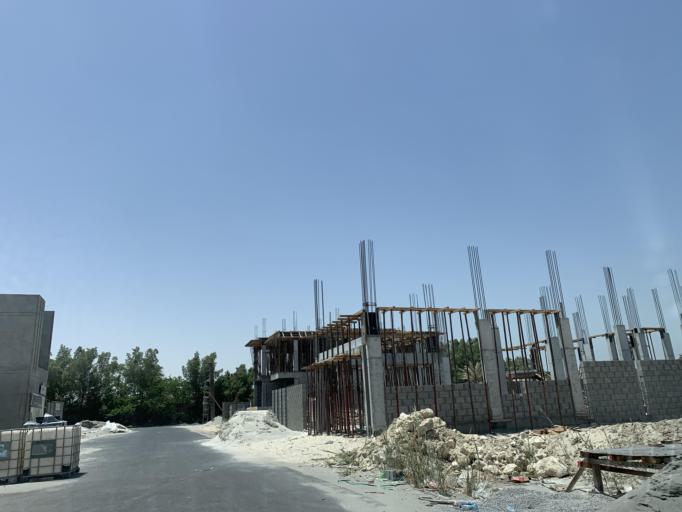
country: BH
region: Manama
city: Jidd Hafs
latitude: 26.2251
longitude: 50.4723
